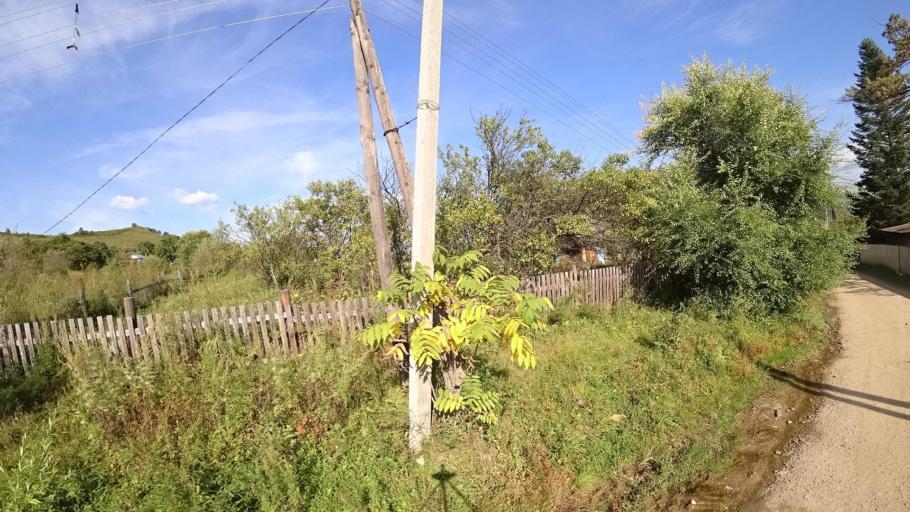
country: RU
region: Jewish Autonomous Oblast
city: Birakan
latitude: 48.9965
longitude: 131.7237
